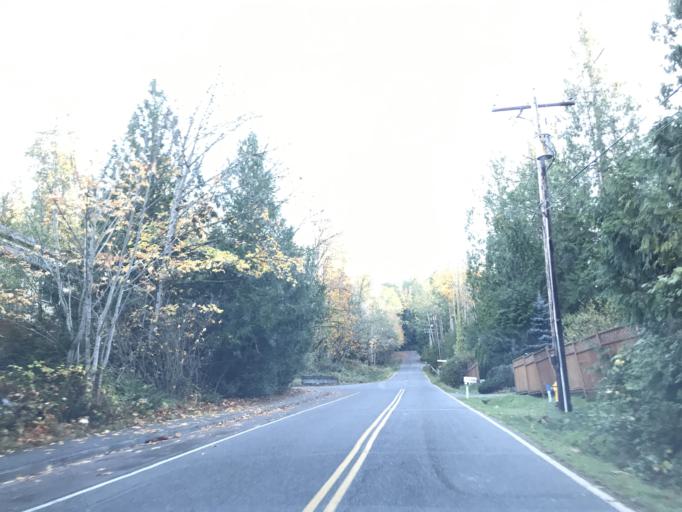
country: US
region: Washington
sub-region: Whatcom County
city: Geneva
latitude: 48.7432
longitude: -122.4099
